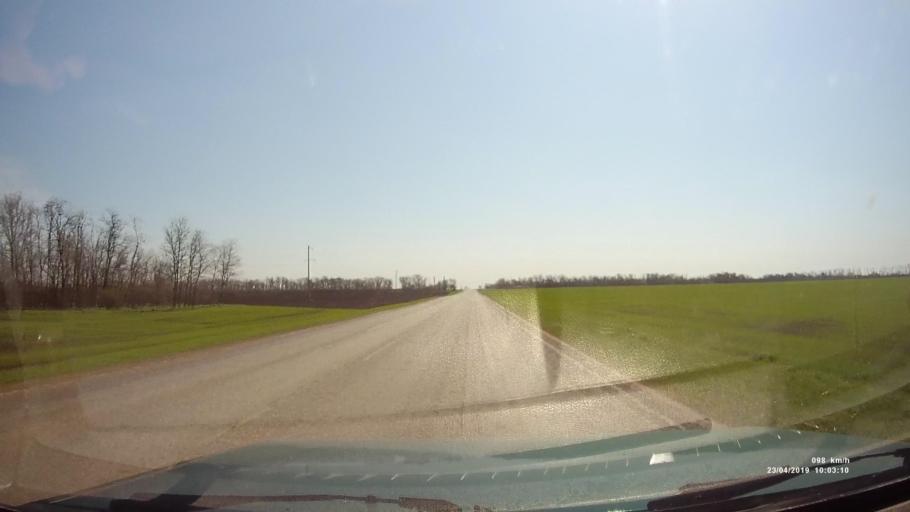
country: RU
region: Rostov
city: Sovetskoye
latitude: 46.7568
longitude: 42.1836
